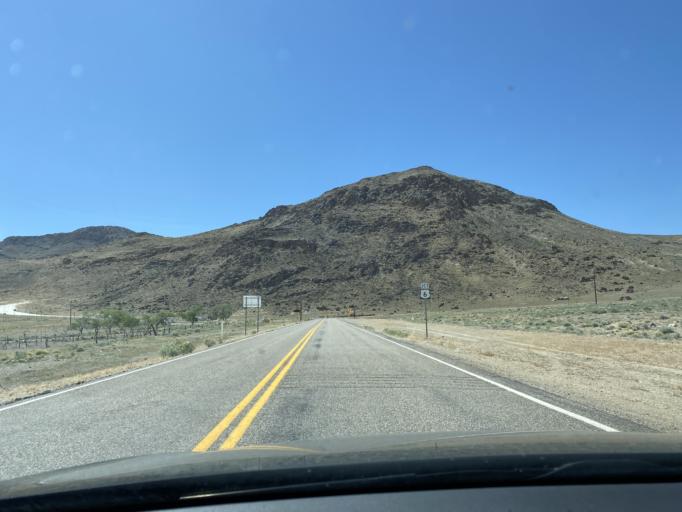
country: US
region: Nevada
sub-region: Nye County
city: Tonopah
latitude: 38.1907
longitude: -116.3657
